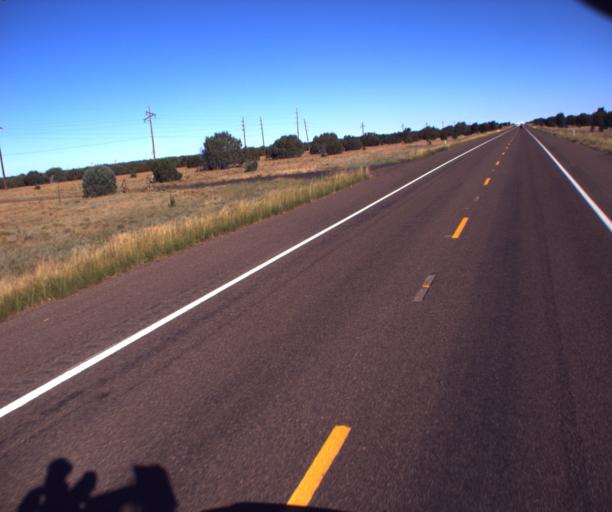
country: US
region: Arizona
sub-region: Navajo County
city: Show Low
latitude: 34.2787
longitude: -110.0264
